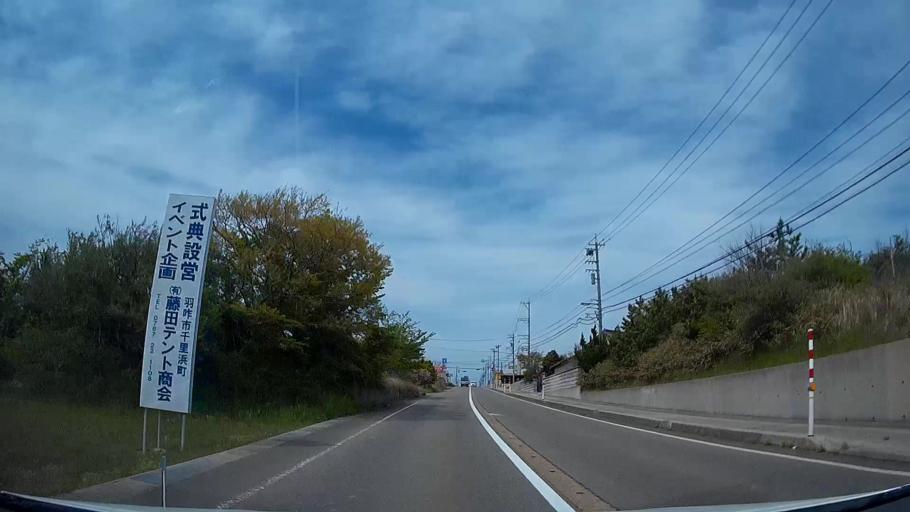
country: JP
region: Ishikawa
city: Hakui
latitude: 36.9864
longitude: 136.7757
